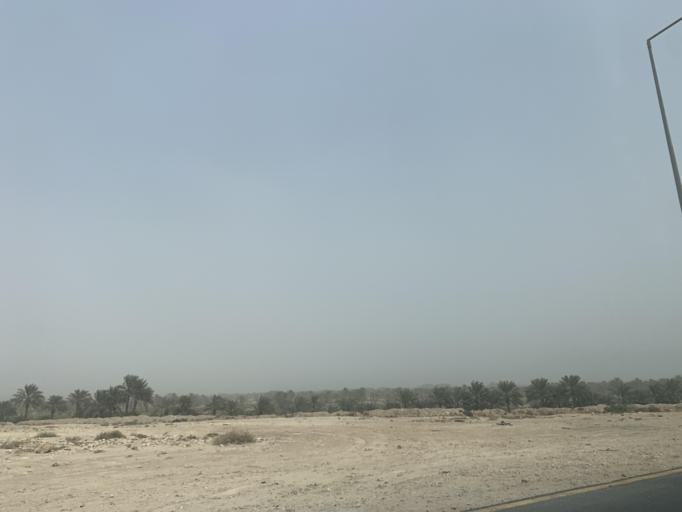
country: BH
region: Central Governorate
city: Madinat Hamad
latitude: 26.1737
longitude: 50.4840
